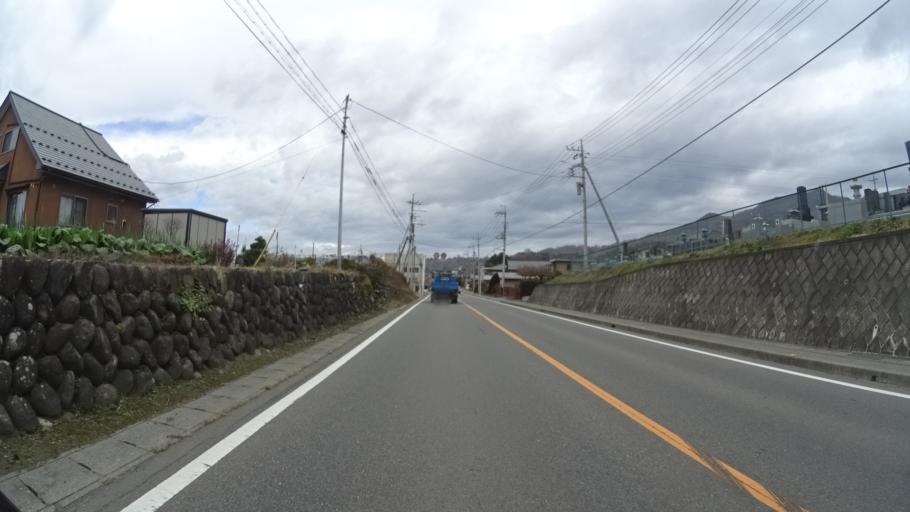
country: JP
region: Gunma
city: Numata
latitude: 36.6624
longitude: 139.1464
